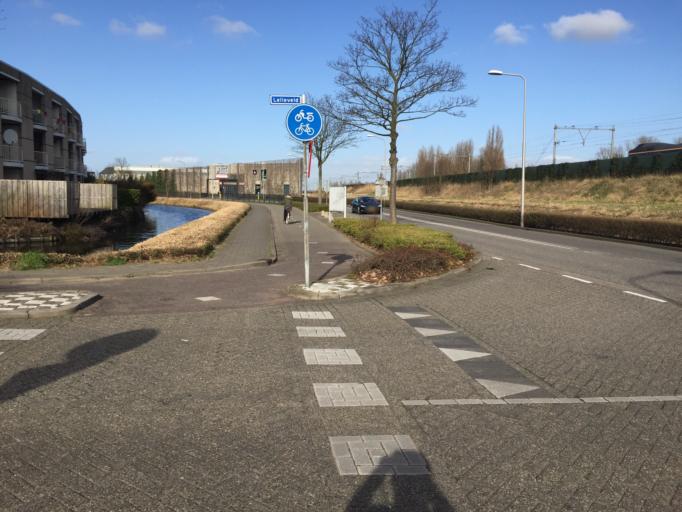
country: NL
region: South Holland
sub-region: Gemeente Krimpen aan den IJssel
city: Krimpen aan den IJssel
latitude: 51.9725
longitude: 4.6245
